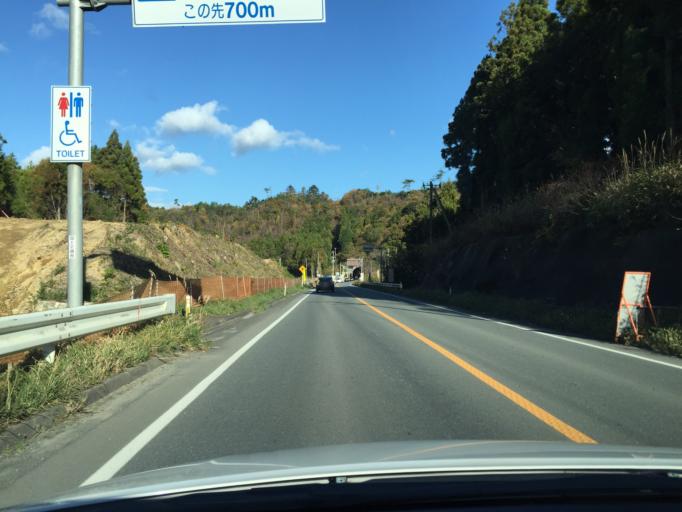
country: JP
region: Fukushima
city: Iwaki
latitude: 37.1587
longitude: 140.9955
